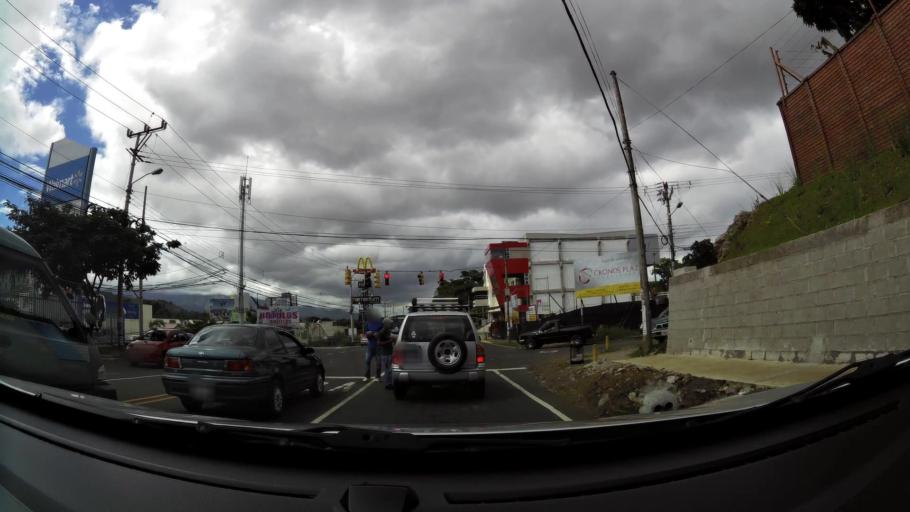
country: CR
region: San Jose
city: Curridabat
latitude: 9.9118
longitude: -84.0163
